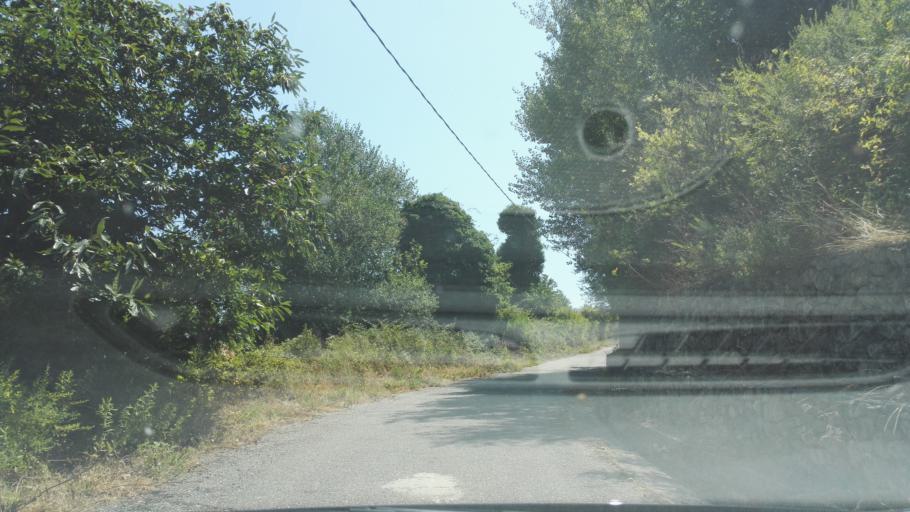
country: IT
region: Calabria
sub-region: Provincia di Reggio Calabria
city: Bivongi
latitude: 38.4901
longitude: 16.4198
